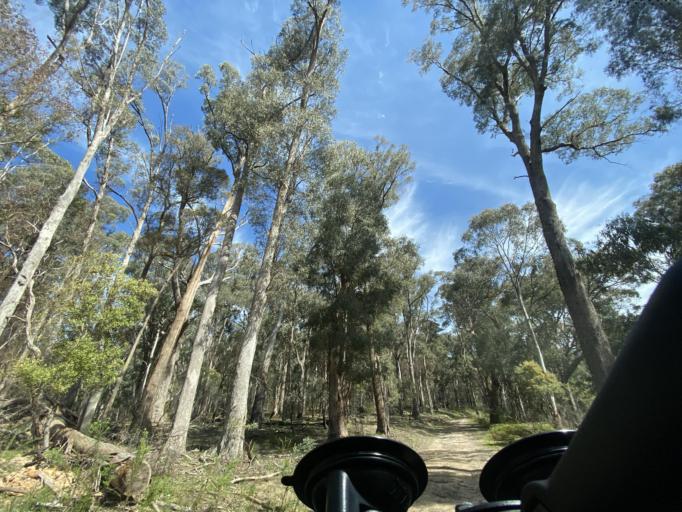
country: AU
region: Victoria
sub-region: Mansfield
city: Mansfield
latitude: -36.8332
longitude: 146.1010
